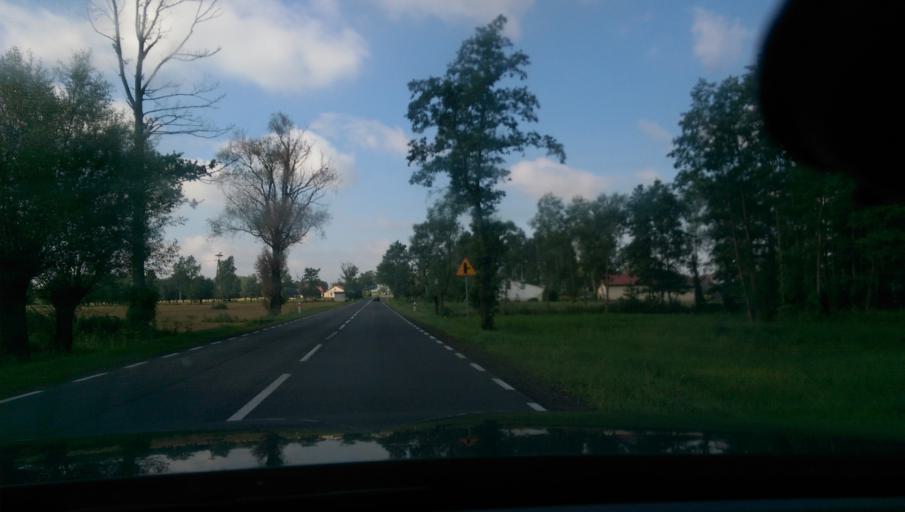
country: PL
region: Masovian Voivodeship
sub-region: Powiat plonski
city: Sochocin
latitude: 52.7087
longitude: 20.4938
